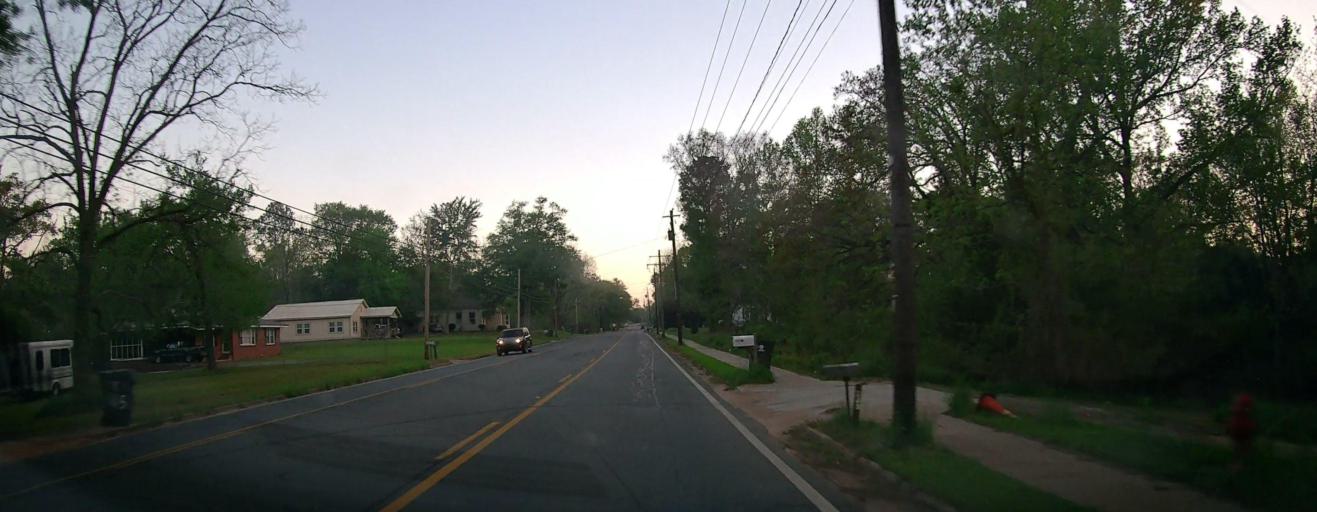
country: US
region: Georgia
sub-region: Marion County
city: Buena Vista
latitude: 32.3130
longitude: -84.5201
